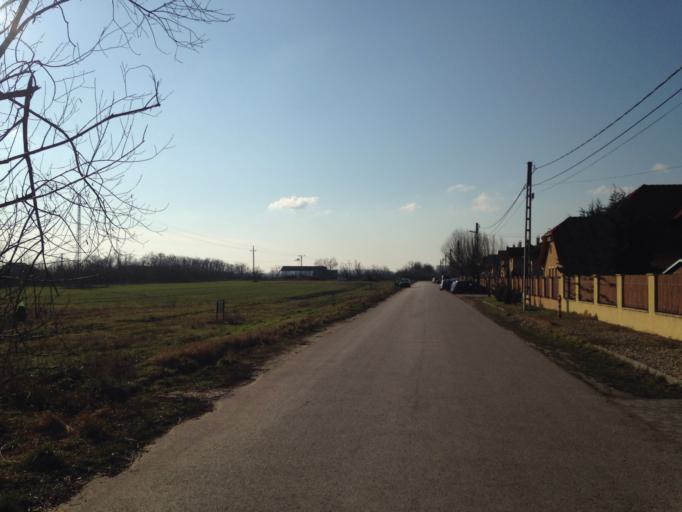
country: HU
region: Pest
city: Dunaharaszti
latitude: 47.3418
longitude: 19.0999
